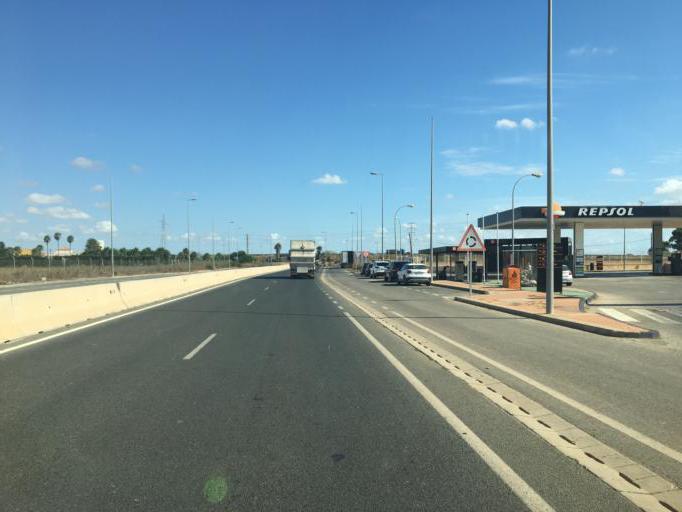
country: ES
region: Murcia
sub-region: Murcia
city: Cartagena
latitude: 37.6537
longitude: -0.9825
